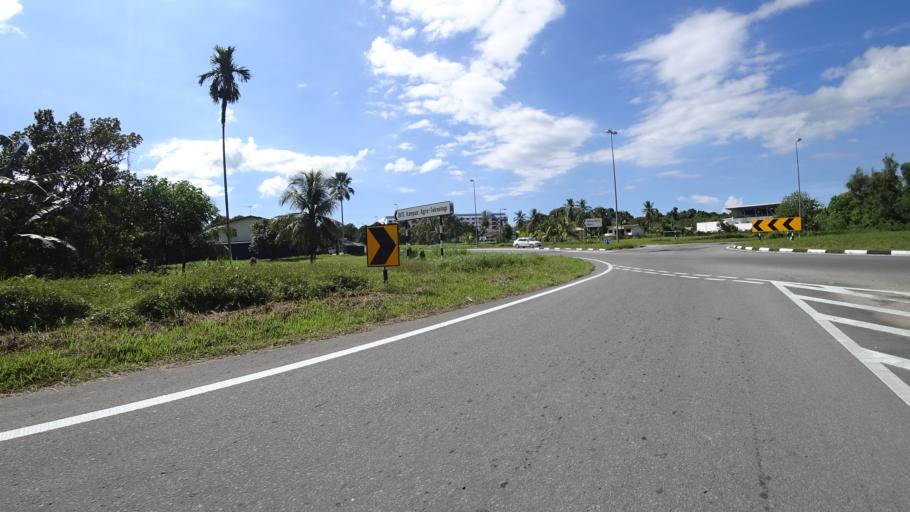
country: BN
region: Tutong
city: Tutong
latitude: 4.7693
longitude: 114.8169
